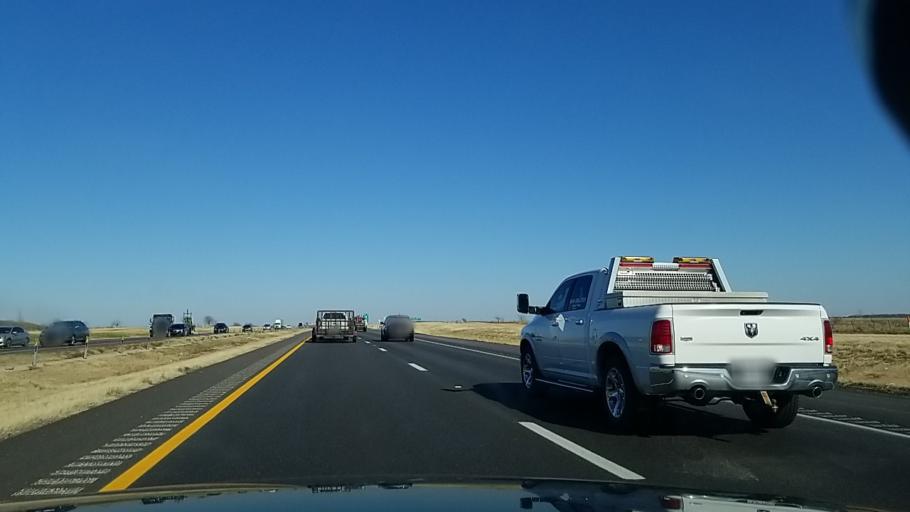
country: US
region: Texas
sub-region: Denton County
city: Northlake
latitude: 33.0820
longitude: -97.2343
